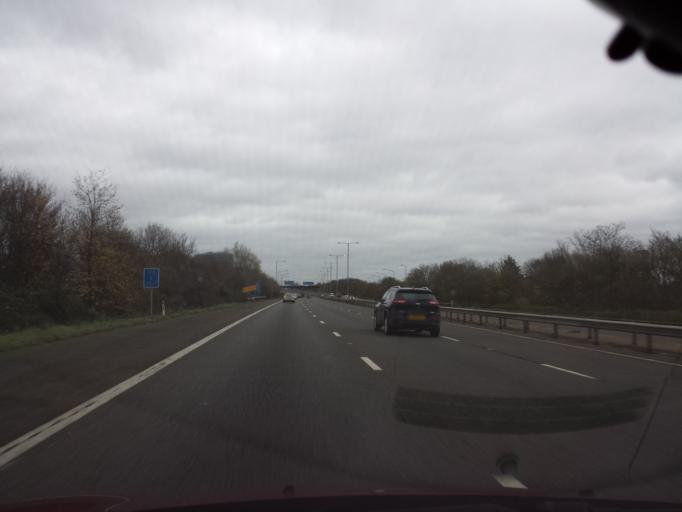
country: GB
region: England
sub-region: Surrey
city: Sunbury-on-Thames
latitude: 51.4151
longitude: -0.4281
